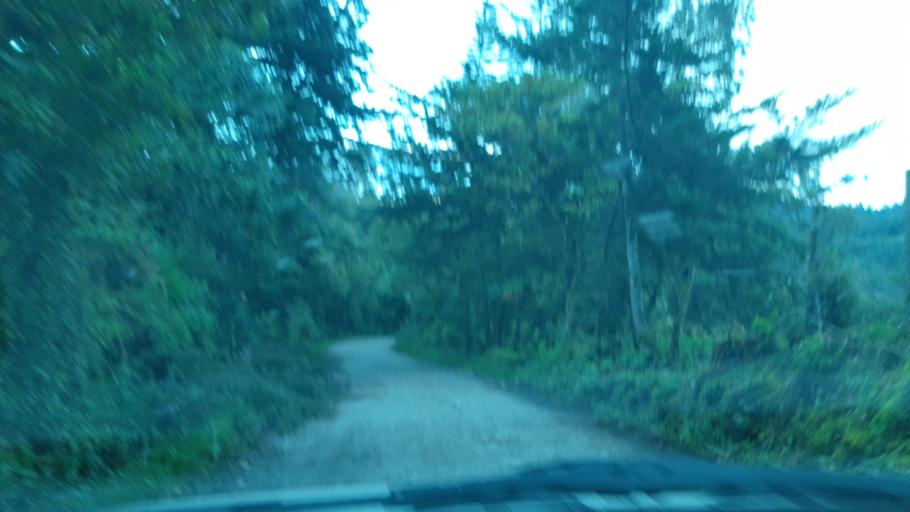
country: CO
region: Boyaca
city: Garagoa
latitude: 5.0920
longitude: -73.3344
